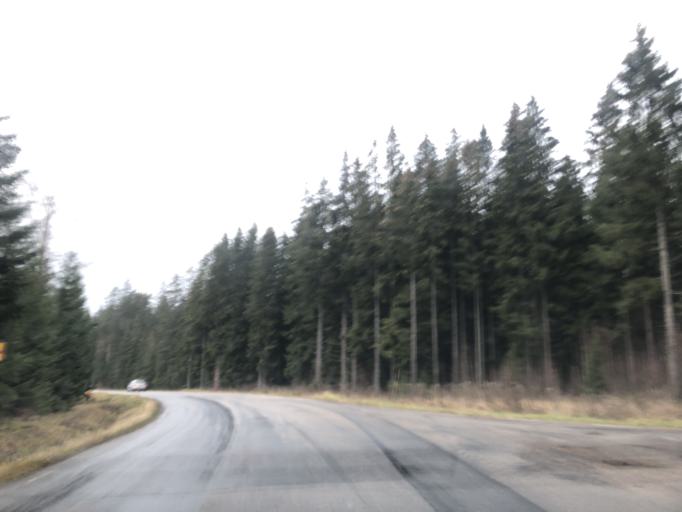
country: SE
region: Vaestra Goetaland
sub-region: Ulricehamns Kommun
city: Ulricehamn
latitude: 57.8971
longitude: 13.4985
